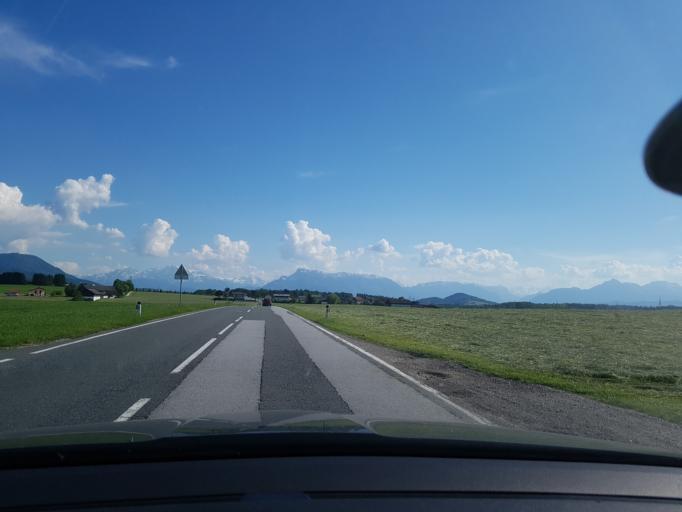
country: AT
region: Salzburg
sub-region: Politischer Bezirk Salzburg-Umgebung
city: Obertrum am See
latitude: 47.9055
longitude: 13.0802
